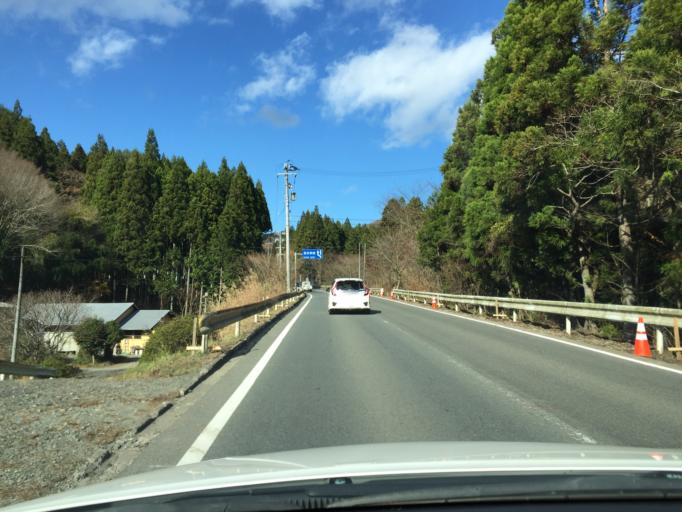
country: JP
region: Fukushima
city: Namie
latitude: 37.6720
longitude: 140.8666
